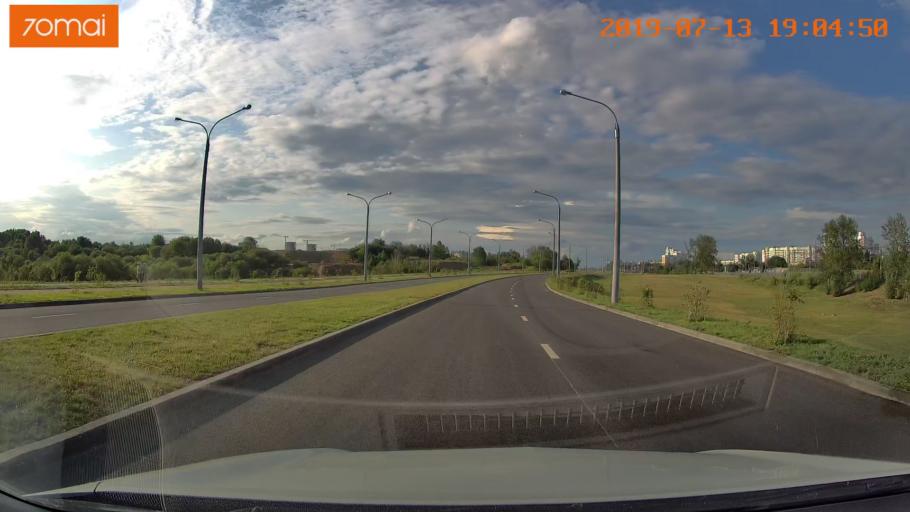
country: BY
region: Minsk
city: Syenitsa
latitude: 53.8553
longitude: 27.5562
